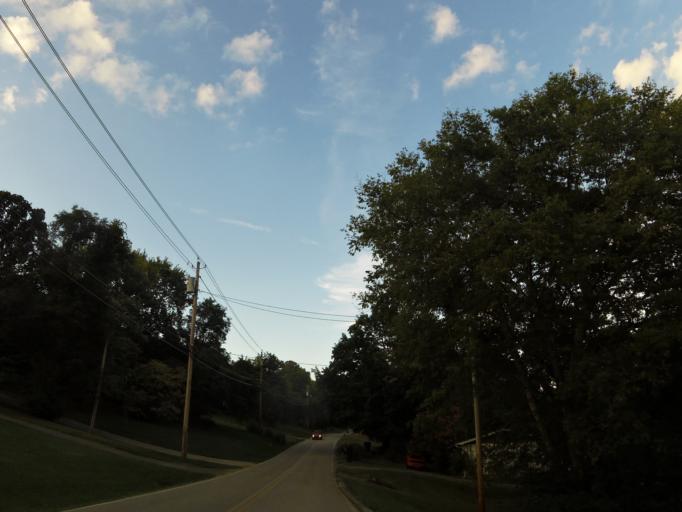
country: US
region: Tennessee
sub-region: Knox County
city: Farragut
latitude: 35.9155
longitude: -84.1644
